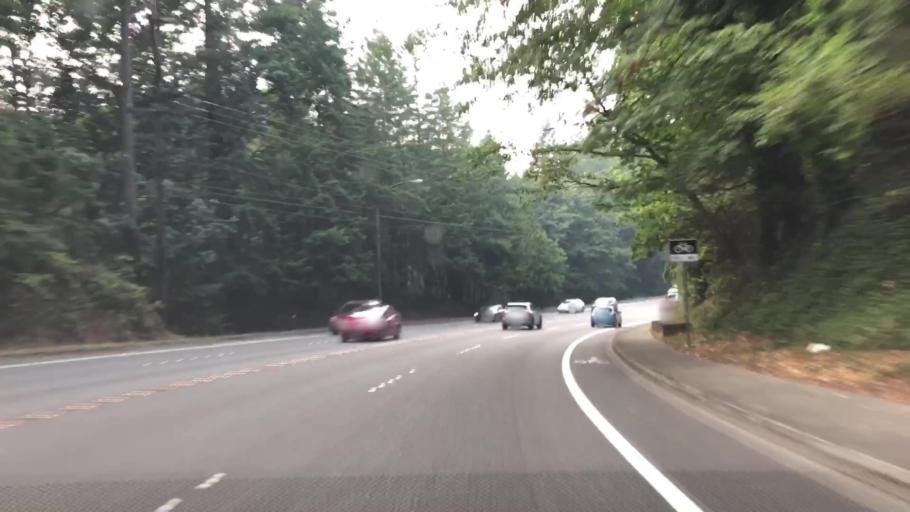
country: US
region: Washington
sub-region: King County
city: Newport
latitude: 47.5592
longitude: -122.1685
